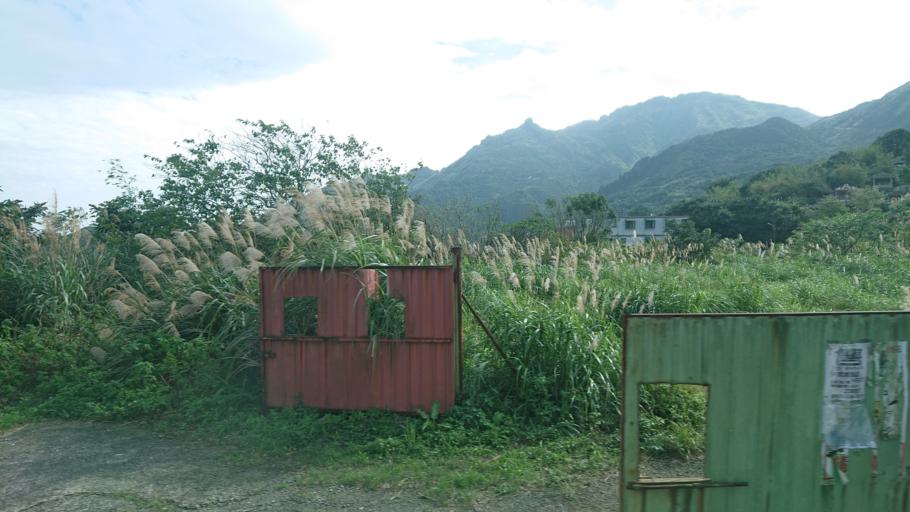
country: TW
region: Taiwan
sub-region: Keelung
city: Keelung
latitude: 25.1085
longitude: 121.8495
